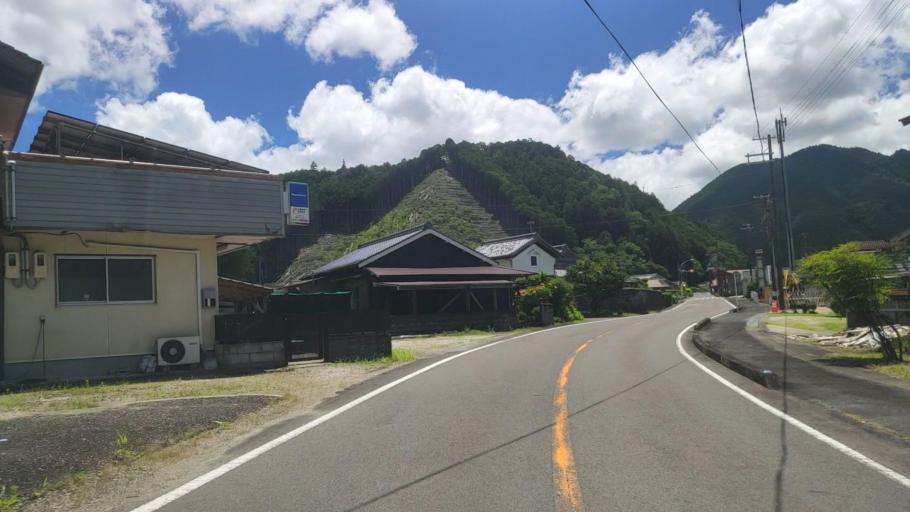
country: JP
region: Mie
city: Owase
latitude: 33.9856
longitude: 136.0482
